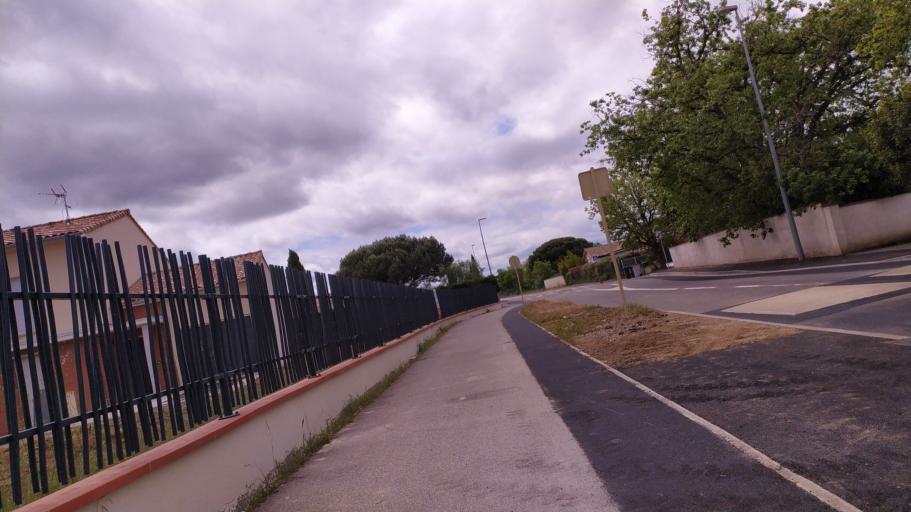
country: FR
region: Midi-Pyrenees
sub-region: Departement de la Haute-Garonne
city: Tournefeuille
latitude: 43.5834
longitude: 1.3072
